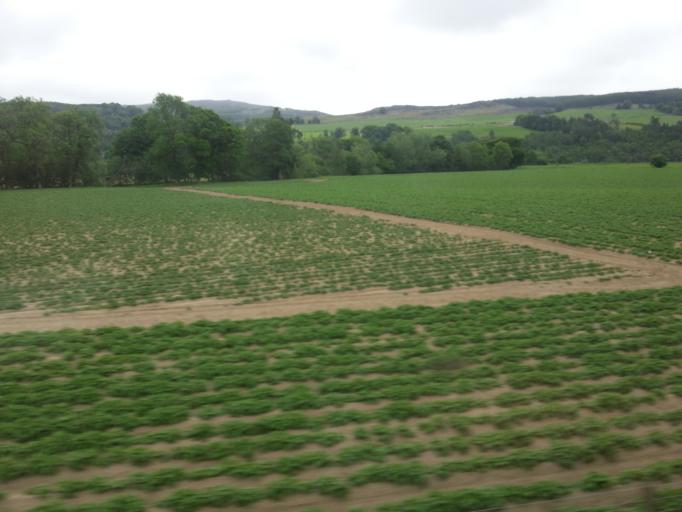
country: GB
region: Scotland
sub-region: Perth and Kinross
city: Pitlochry
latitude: 56.6088
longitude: -3.6400
